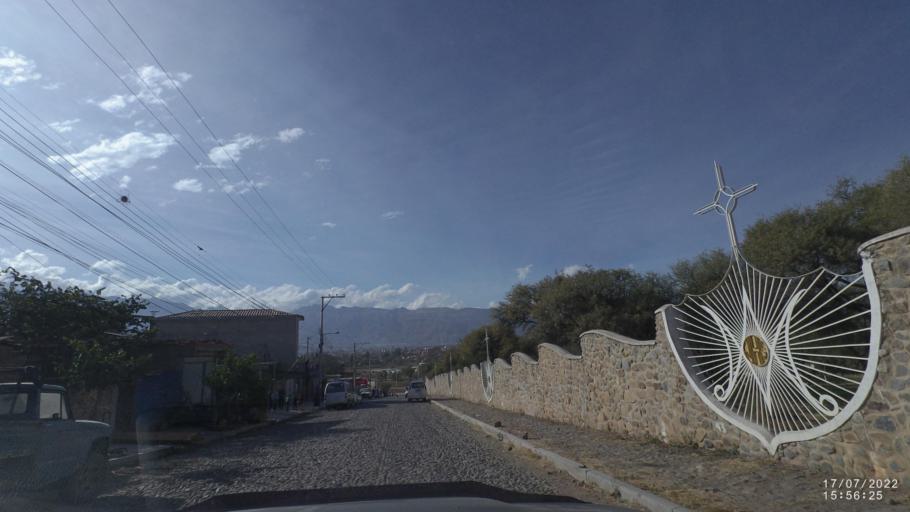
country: BO
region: Cochabamba
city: Sipe Sipe
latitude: -17.4220
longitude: -66.2849
